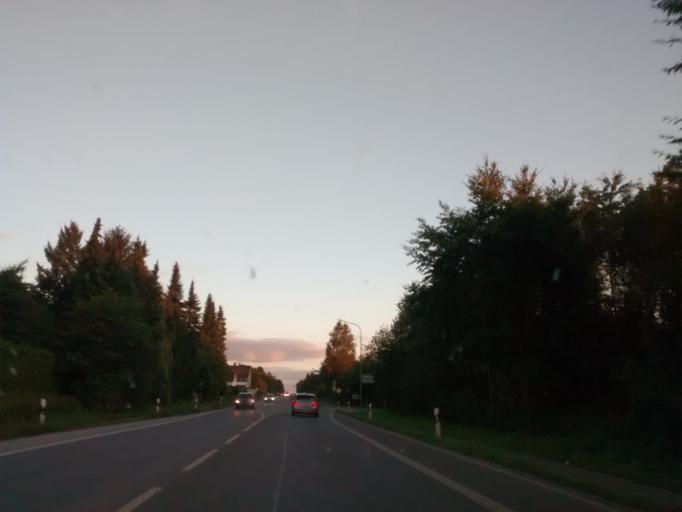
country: DE
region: North Rhine-Westphalia
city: Halle
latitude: 52.0416
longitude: 8.3888
